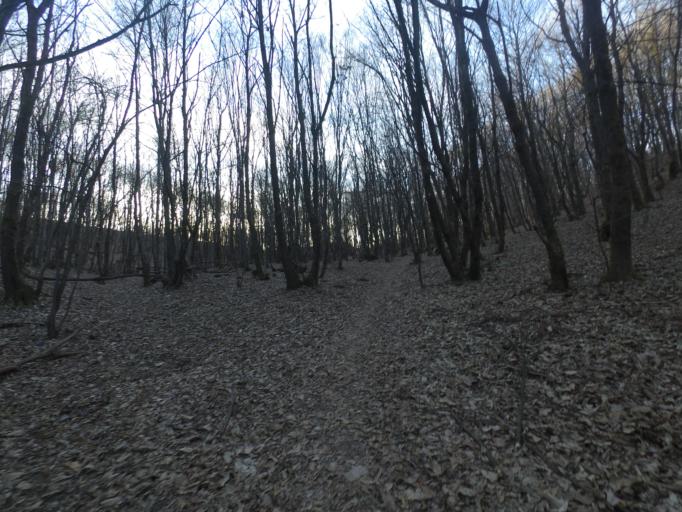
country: HR
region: Karlovacka
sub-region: Grad Karlovac
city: Karlovac
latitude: 45.4762
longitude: 15.5303
